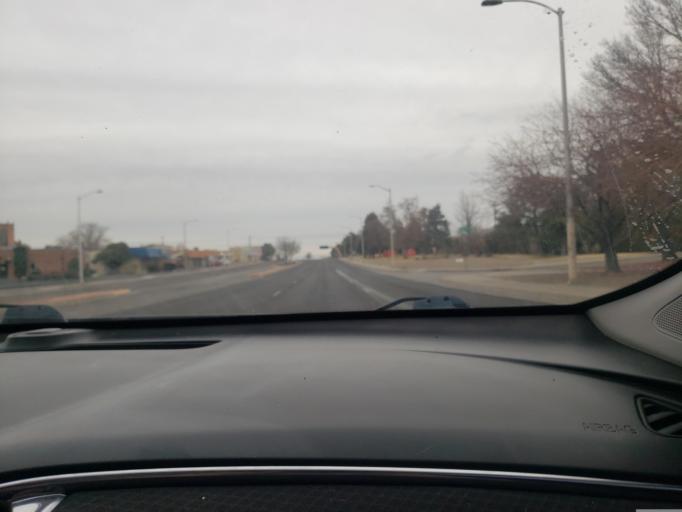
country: US
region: New Mexico
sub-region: Bernalillo County
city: Albuquerque
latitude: 35.0962
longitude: -106.5862
